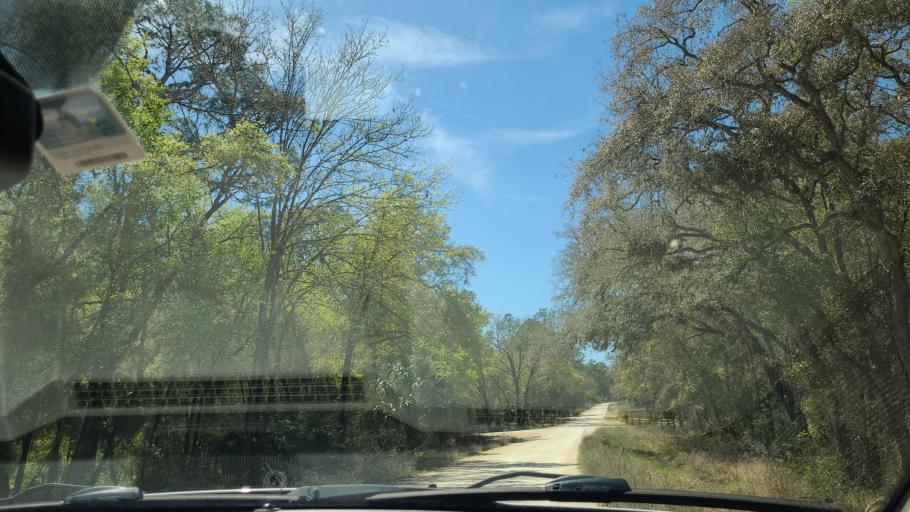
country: US
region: Florida
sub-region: Putnam County
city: Interlachen
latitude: 29.4297
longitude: -81.7877
